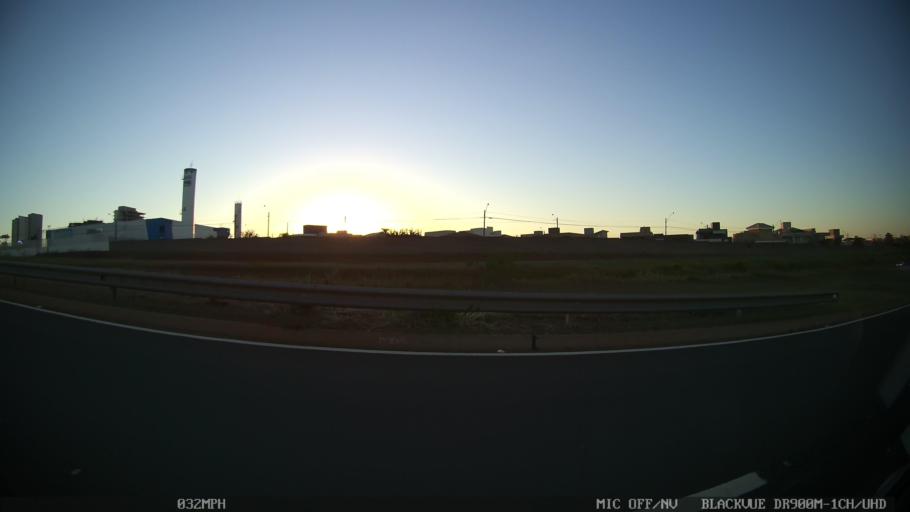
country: BR
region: Sao Paulo
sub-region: Sao Jose Do Rio Preto
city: Sao Jose do Rio Preto
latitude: -20.8640
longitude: -49.4096
